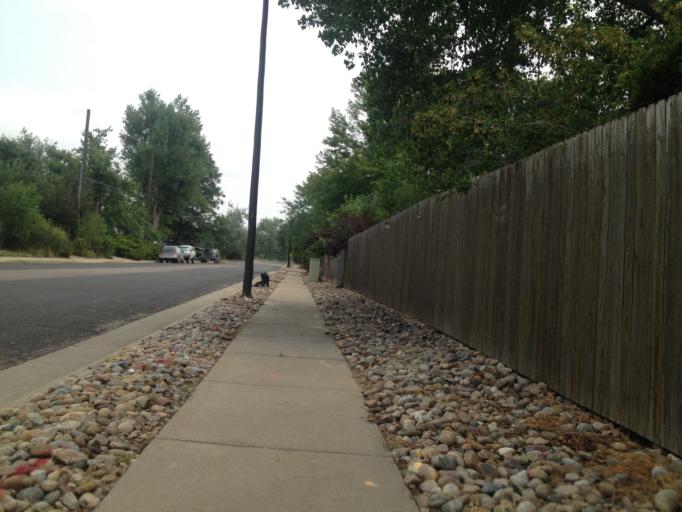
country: US
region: Colorado
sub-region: Boulder County
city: Louisville
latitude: 39.9687
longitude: -105.1349
